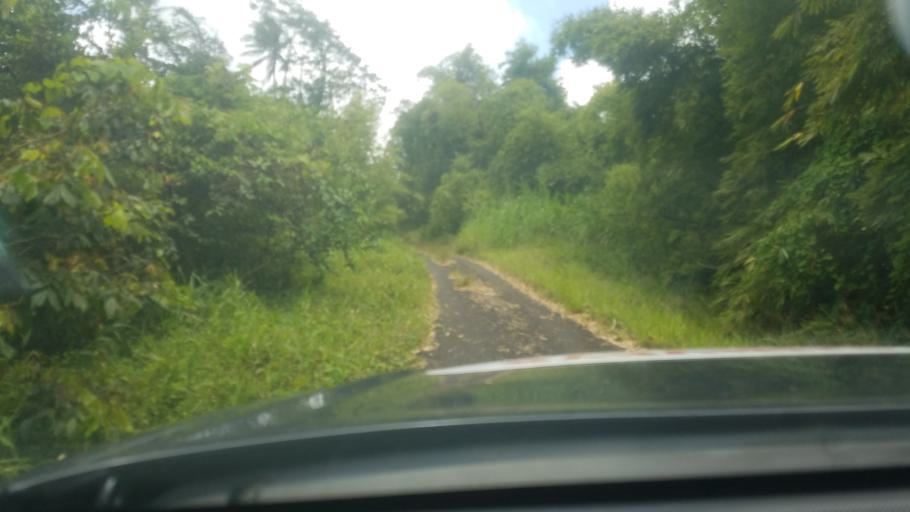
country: LC
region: Anse-la-Raye
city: Anse La Raye
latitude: 13.9116
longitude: -61.0058
